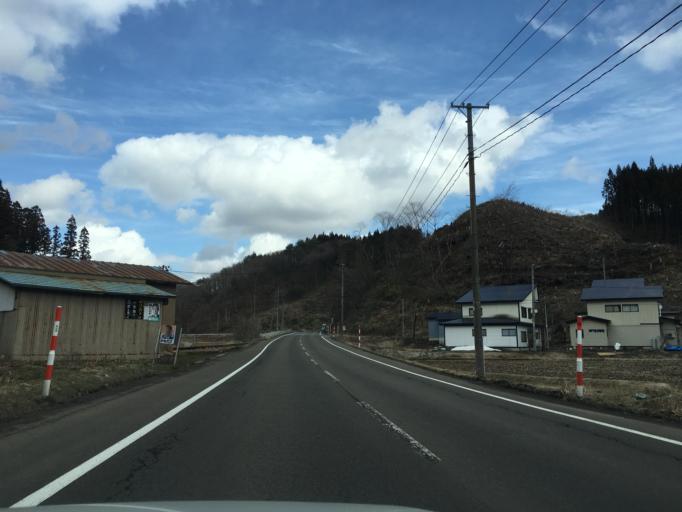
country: JP
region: Akita
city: Odate
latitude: 40.1811
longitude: 140.4979
